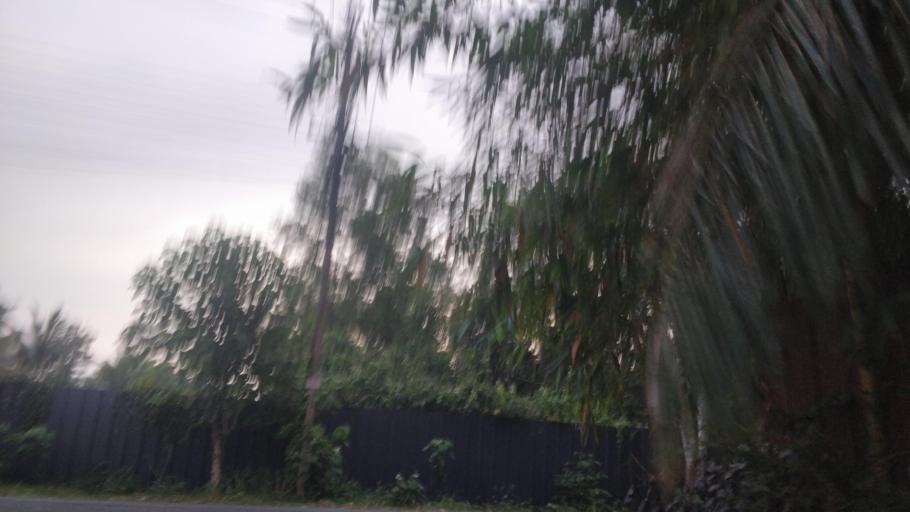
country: IN
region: Kerala
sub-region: Alappuzha
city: Shertallai
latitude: 9.6421
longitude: 76.3283
